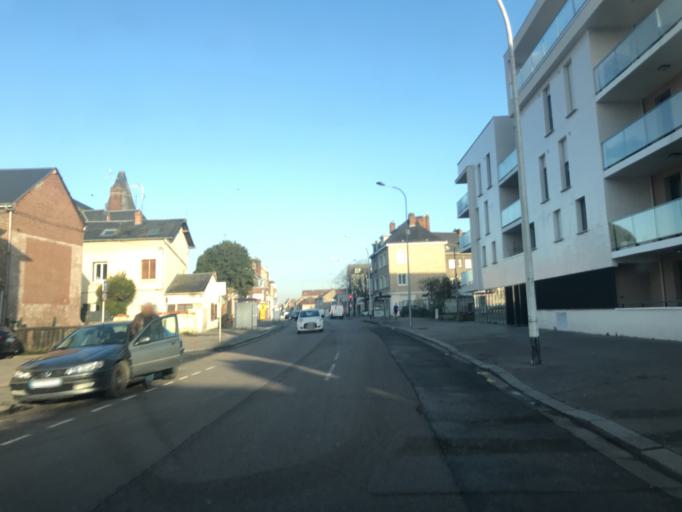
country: FR
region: Haute-Normandie
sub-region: Departement de la Seine-Maritime
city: Sotteville-les-Rouen
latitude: 49.4203
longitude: 1.0939
